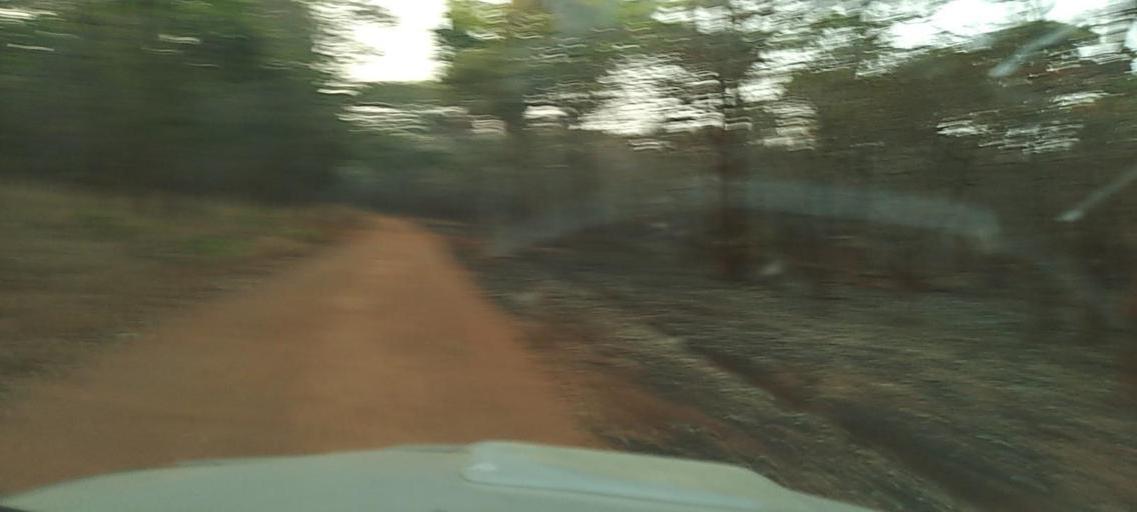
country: ZM
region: North-Western
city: Kasempa
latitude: -13.1003
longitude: 26.4036
